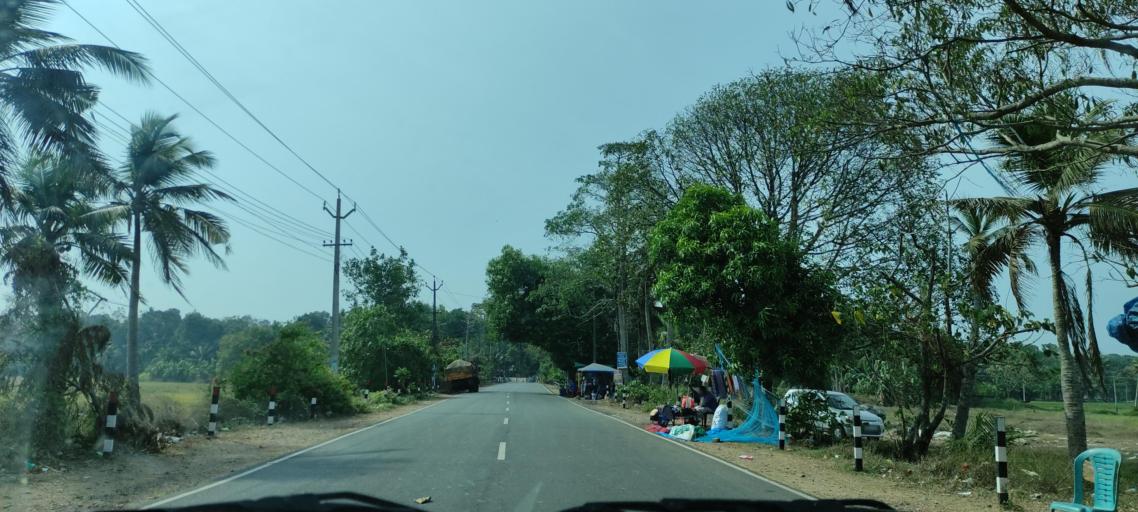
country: IN
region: Kerala
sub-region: Kottayam
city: Vaikam
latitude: 9.6933
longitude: 76.4898
